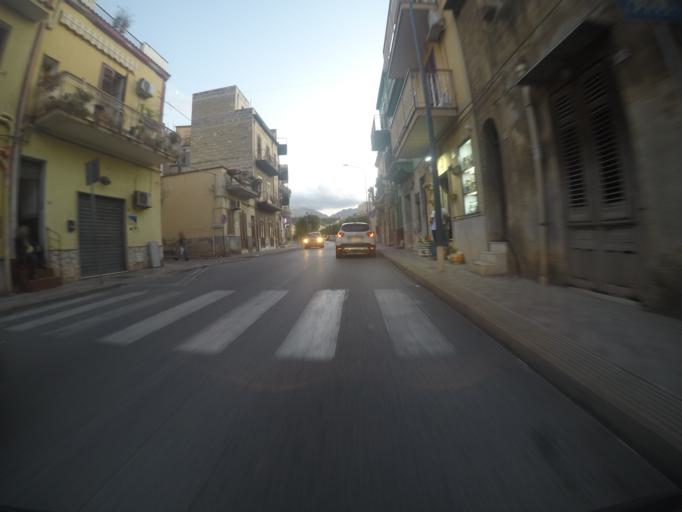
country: IT
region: Sicily
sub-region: Palermo
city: Capaci
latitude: 38.1736
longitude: 13.2407
